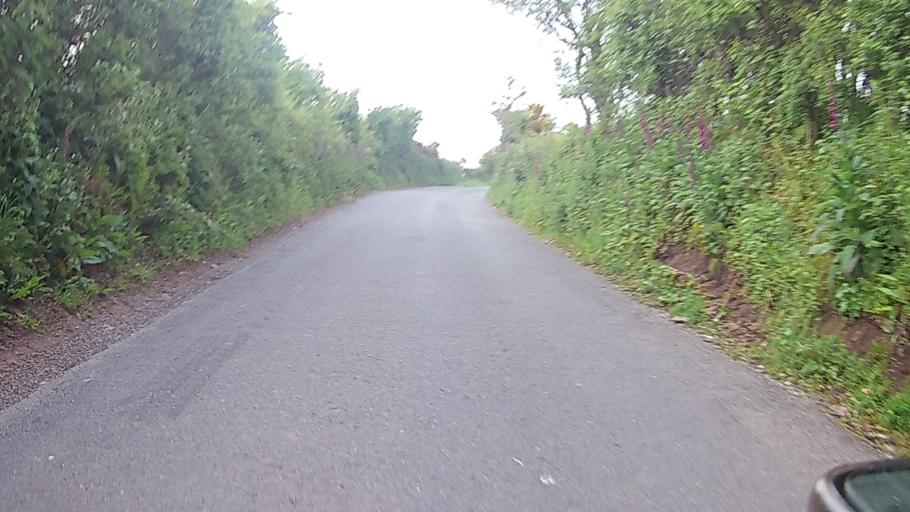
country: IE
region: Munster
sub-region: County Cork
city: Watergrasshill
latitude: 51.9692
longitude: -8.4115
